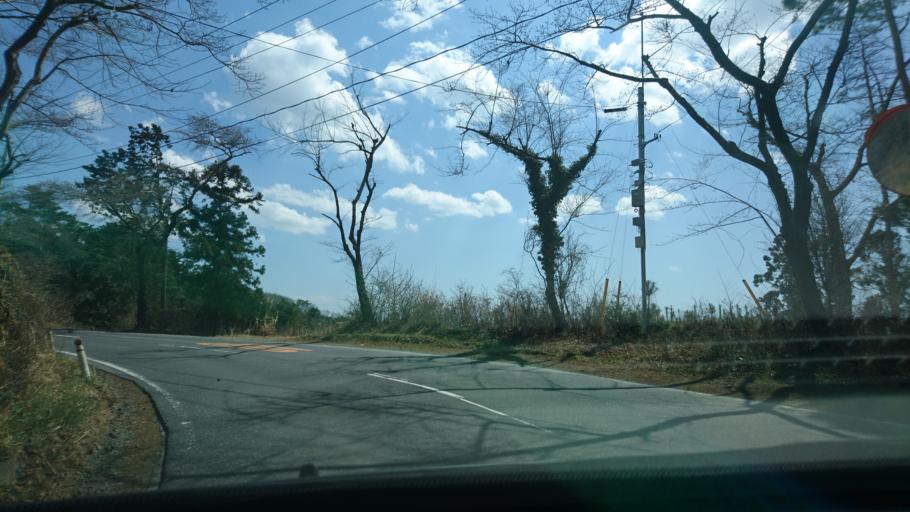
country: JP
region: Miyagi
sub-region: Oshika Gun
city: Onagawa Cho
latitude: 38.4395
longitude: 141.4812
